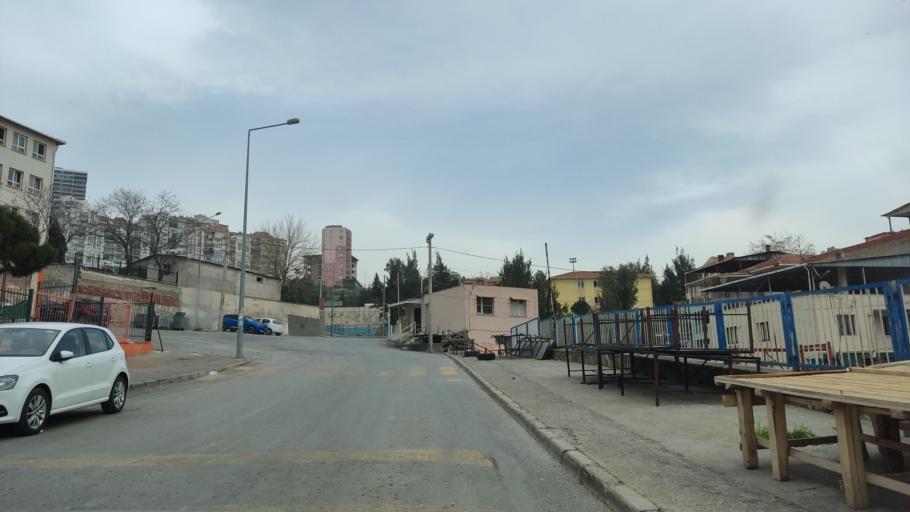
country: TR
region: Izmir
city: Karsiyaka
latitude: 38.5029
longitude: 27.0753
